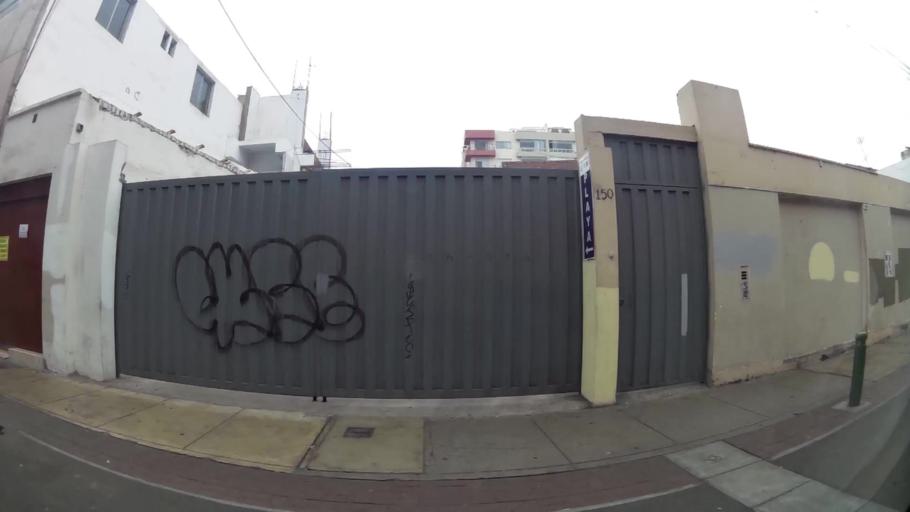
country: PE
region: Lima
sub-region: Lima
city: San Isidro
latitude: -12.1199
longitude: -77.0277
